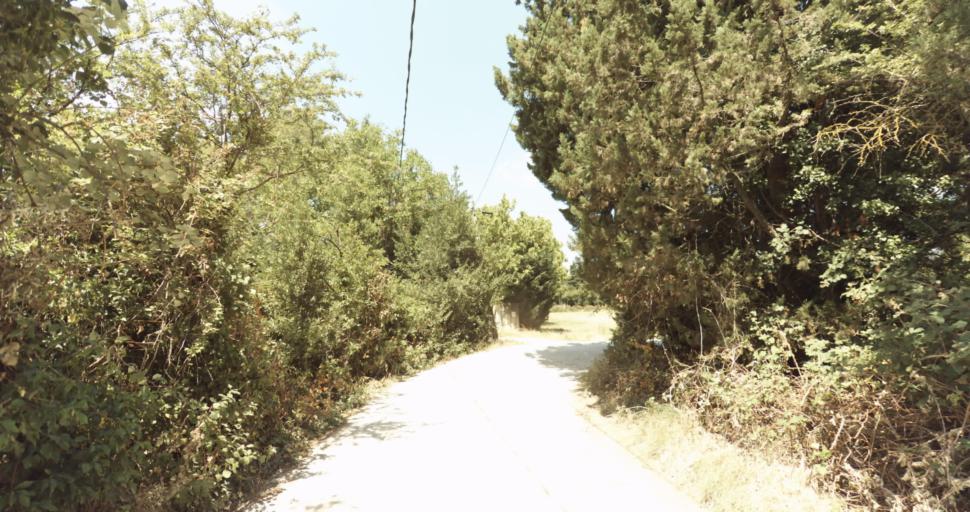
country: FR
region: Provence-Alpes-Cote d'Azur
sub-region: Departement du Vaucluse
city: Monteux
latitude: 44.0105
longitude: 5.0077
